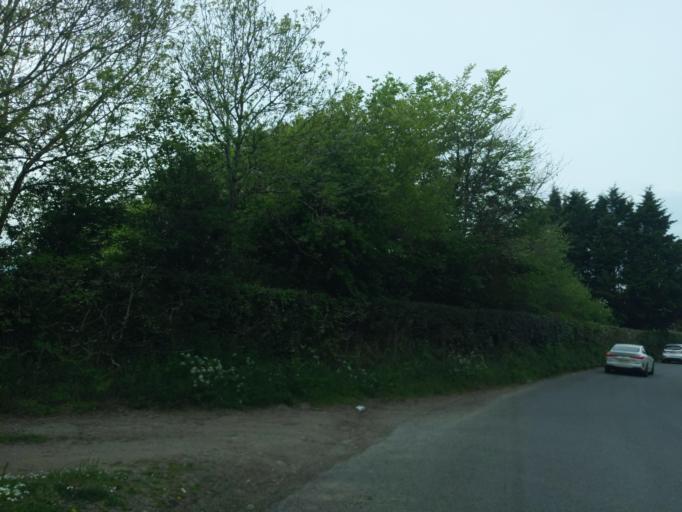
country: GB
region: England
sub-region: Devon
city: Plympton
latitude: 50.4217
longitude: -4.0476
